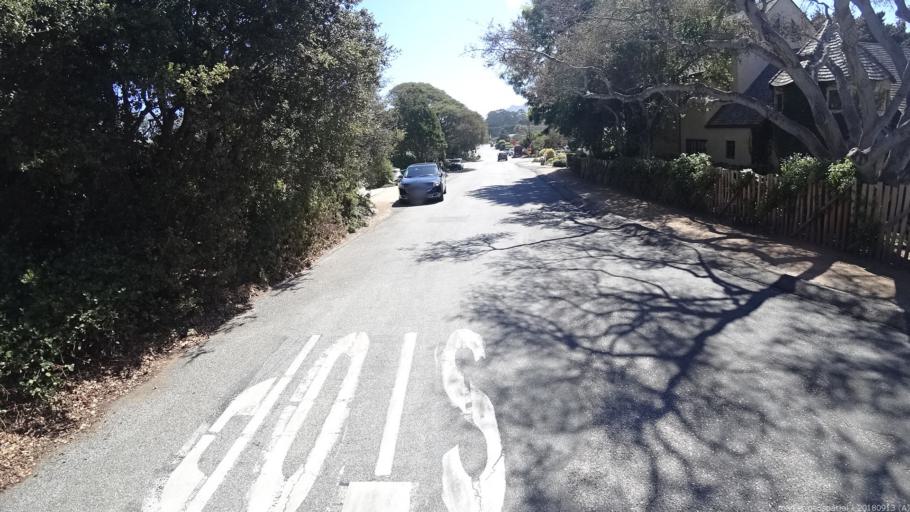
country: US
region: California
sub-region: Monterey County
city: Carmel-by-the-Sea
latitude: 36.5439
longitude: -121.9275
